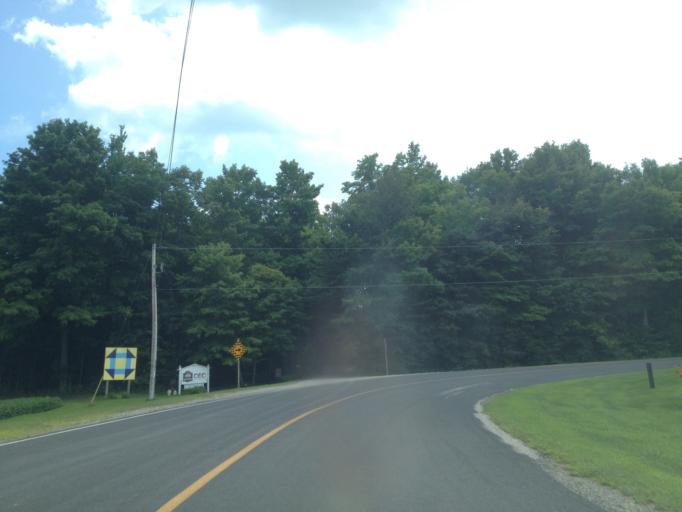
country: CA
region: Ontario
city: Aylmer
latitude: 42.6772
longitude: -81.0181
